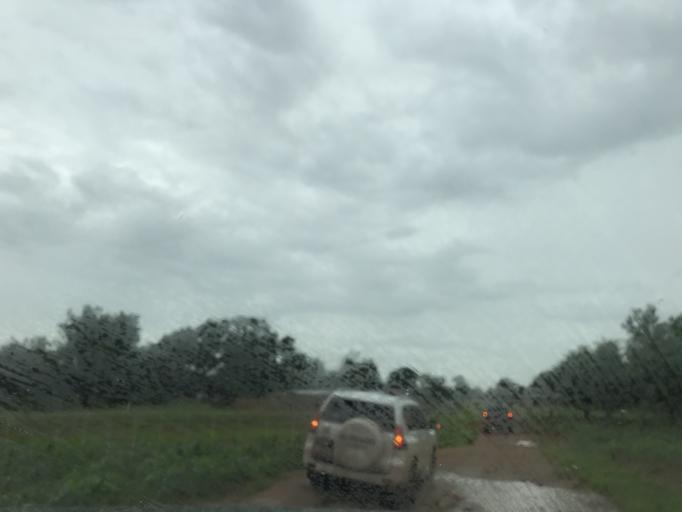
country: GH
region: Upper West
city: Wa
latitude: 10.5136
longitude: -2.7066
